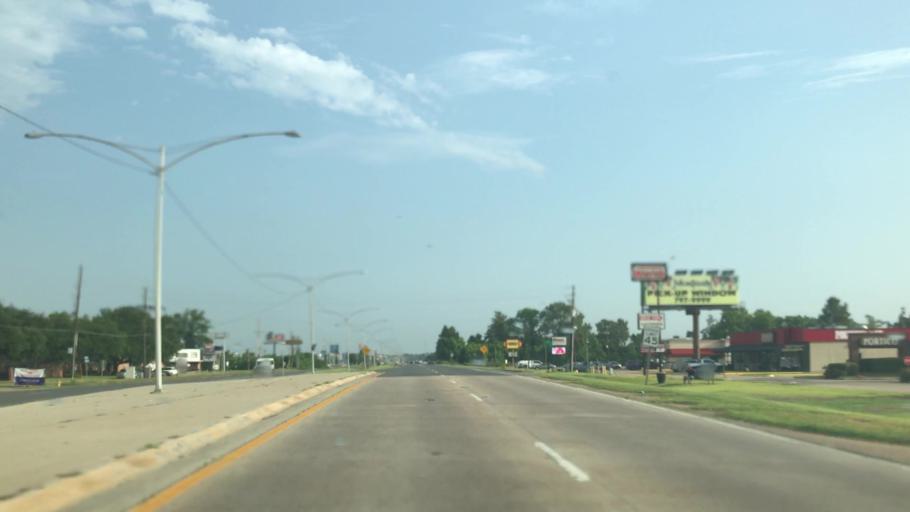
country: US
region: Louisiana
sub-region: Bossier Parish
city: Bossier City
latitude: 32.4325
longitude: -93.7122
